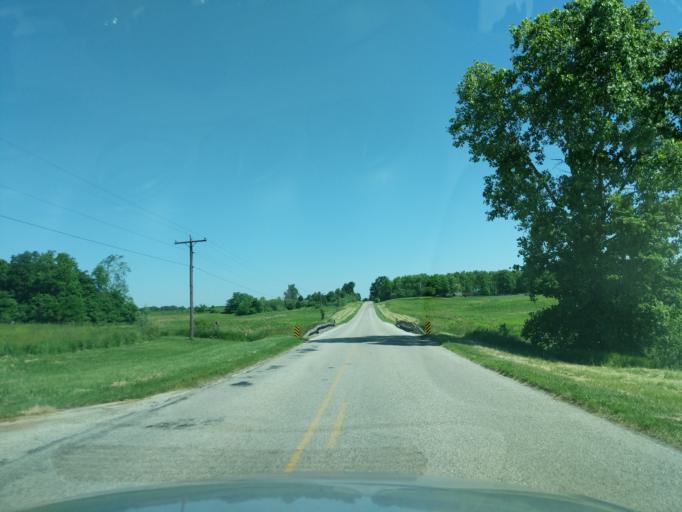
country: US
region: Indiana
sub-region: Huntington County
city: Huntington
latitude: 40.8335
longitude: -85.5087
